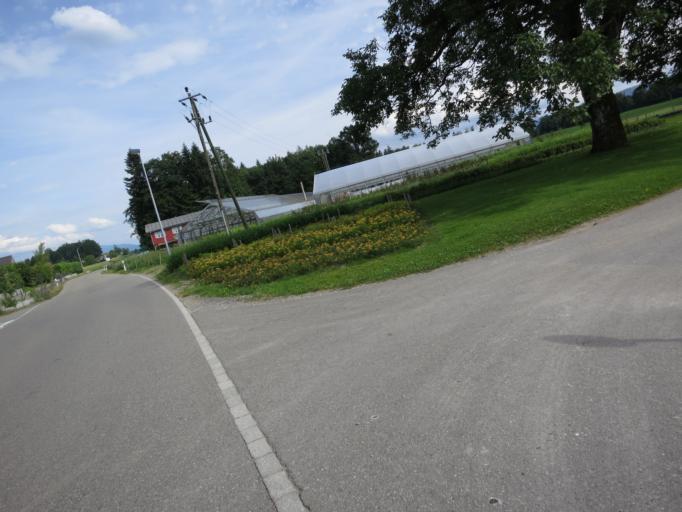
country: CH
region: Zurich
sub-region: Bezirk Hinwil
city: Wolfhausen
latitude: 47.2536
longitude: 8.8048
